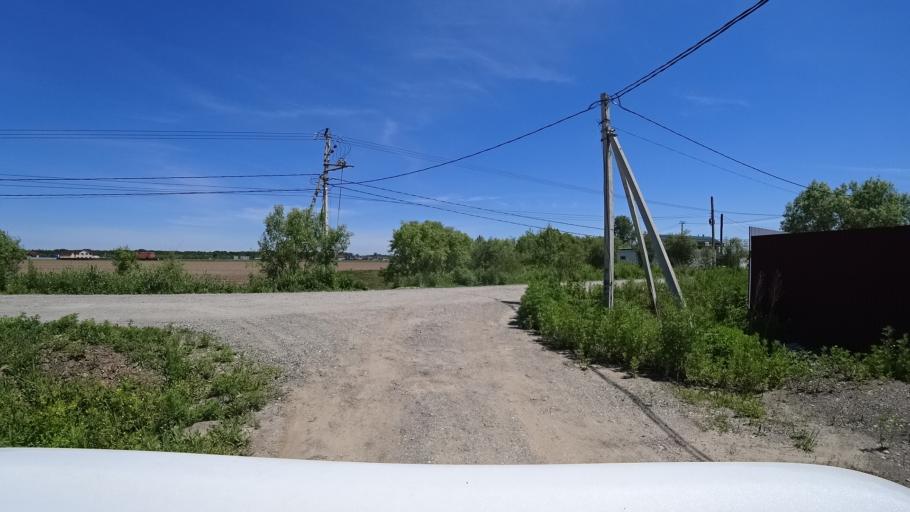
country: RU
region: Khabarovsk Krai
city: Topolevo
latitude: 48.5100
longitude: 135.1850
